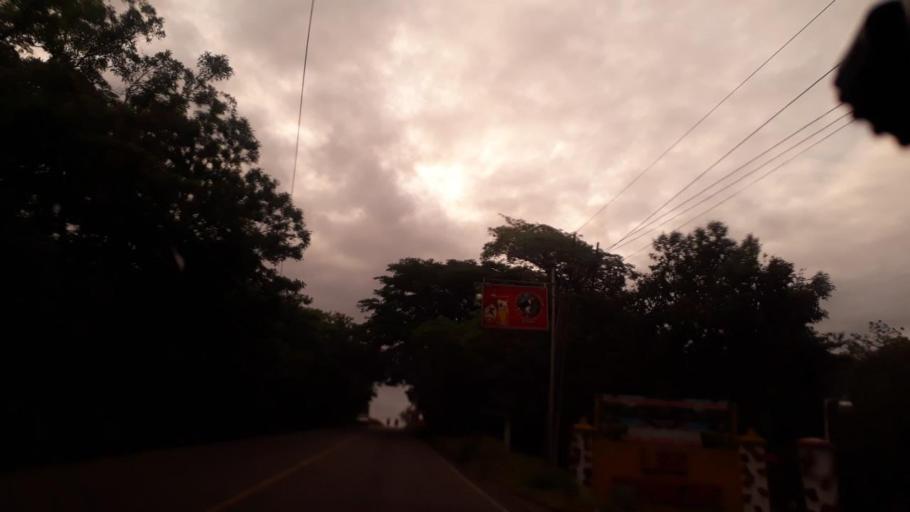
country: GT
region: Jutiapa
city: Jutiapa
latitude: 14.3005
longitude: -89.8844
